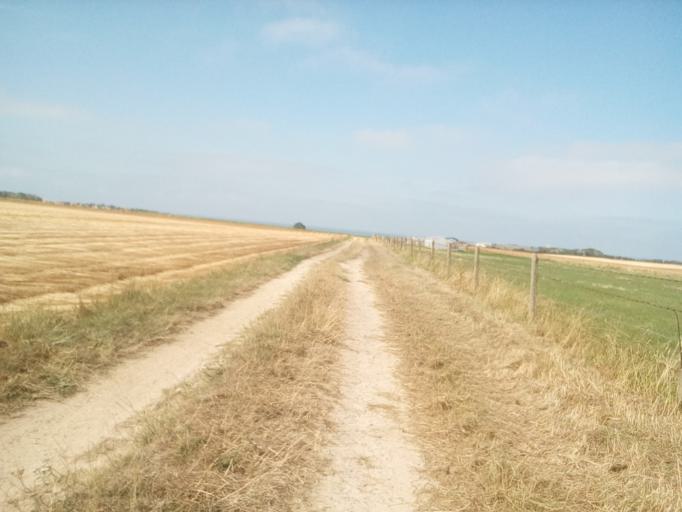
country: FR
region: Lower Normandy
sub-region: Departement du Calvados
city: Bernieres-sur-Mer
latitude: 49.3144
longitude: -0.4391
